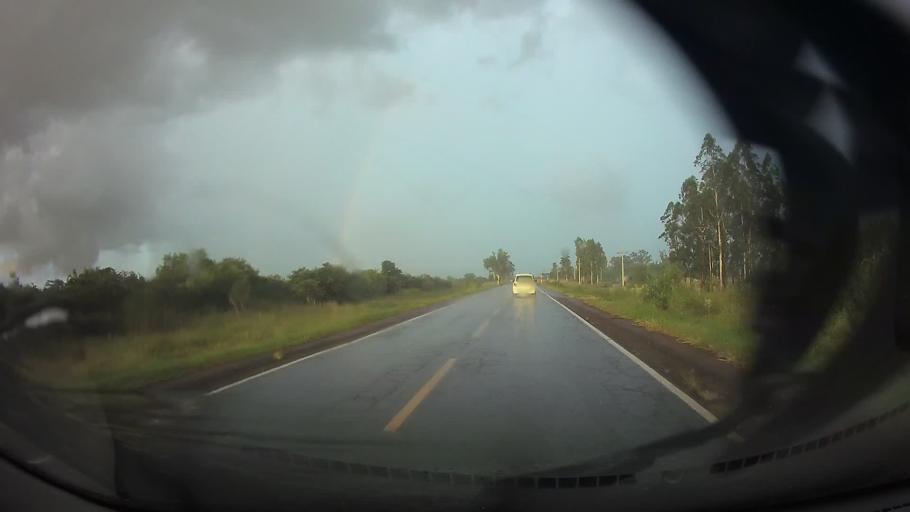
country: PY
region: Paraguari
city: Paraguari
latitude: -25.6969
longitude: -57.1740
